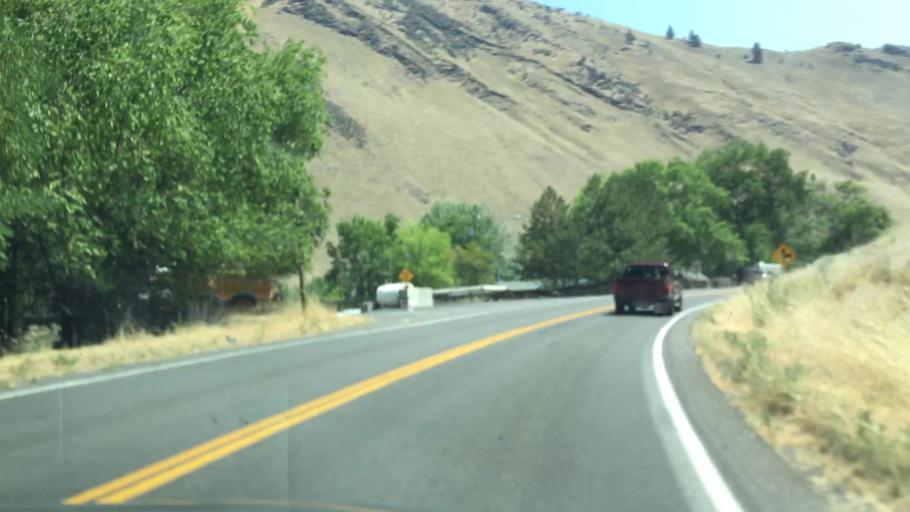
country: US
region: Idaho
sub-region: Idaho County
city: Grangeville
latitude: 45.4311
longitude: -116.3141
